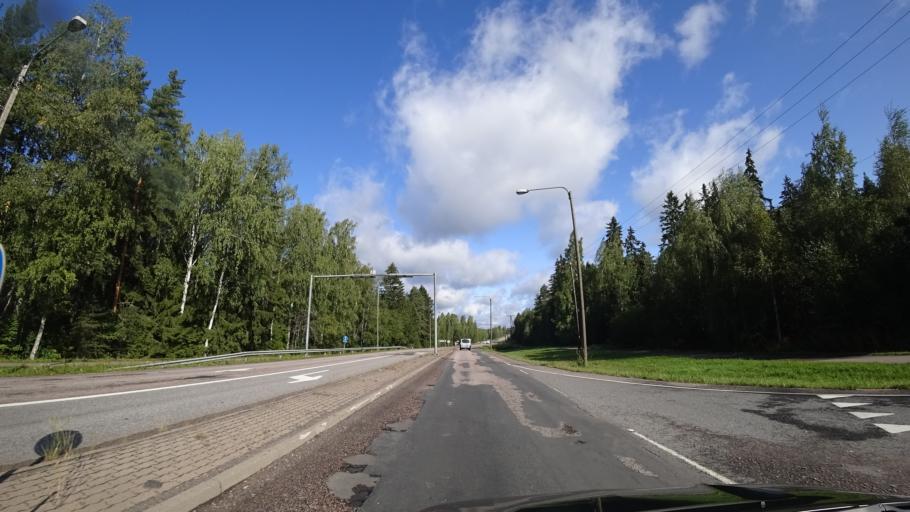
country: FI
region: Uusimaa
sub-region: Helsinki
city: Tuusula
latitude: 60.4152
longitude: 25.0016
